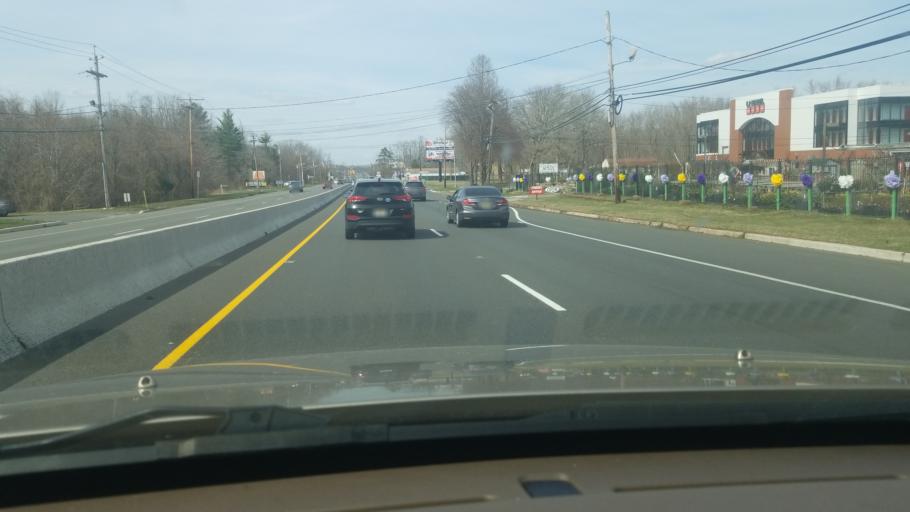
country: US
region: New Jersey
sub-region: Monmouth County
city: West Freehold
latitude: 40.1919
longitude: -74.2518
